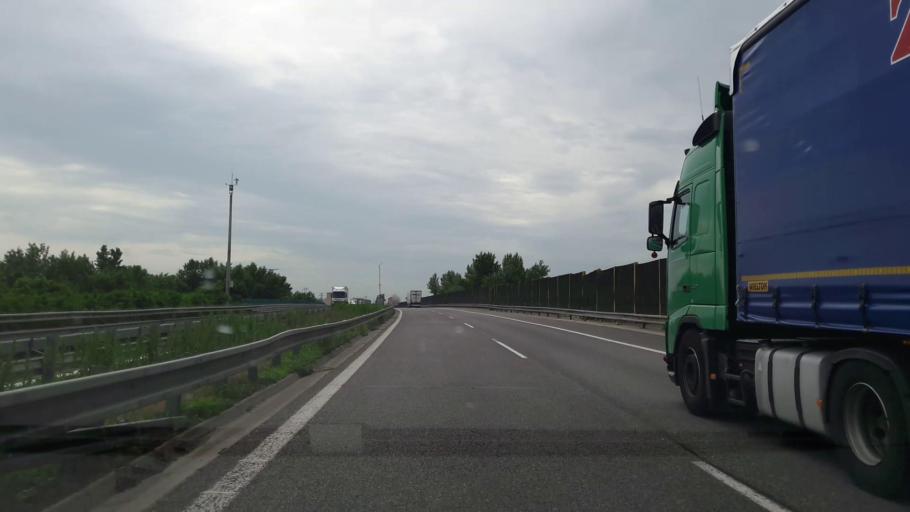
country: AT
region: Burgenland
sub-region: Politischer Bezirk Neusiedl am See
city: Kittsee
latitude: 48.1088
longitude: 17.0865
